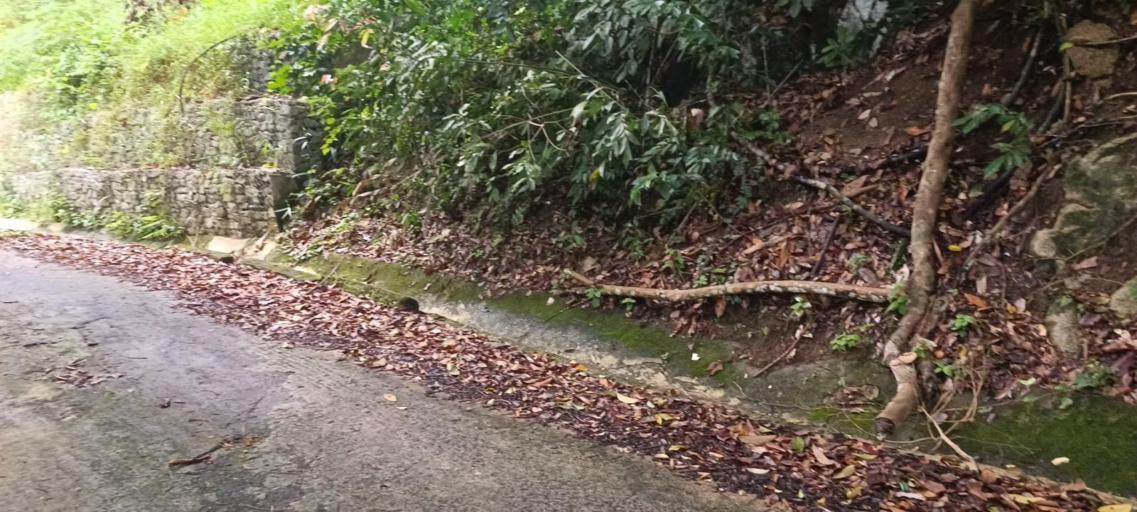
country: MY
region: Penang
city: Kampung Sungai Ara
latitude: 5.3899
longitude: 100.2605
